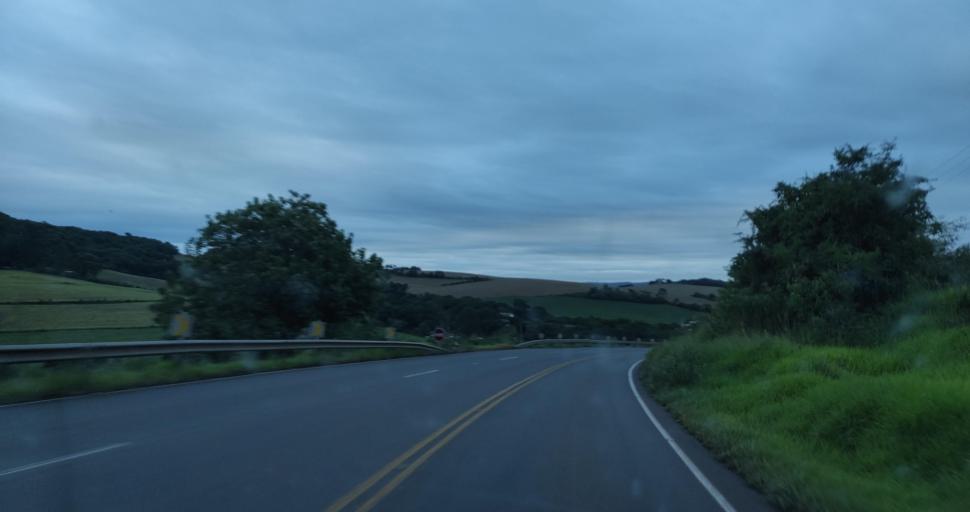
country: BR
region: Santa Catarina
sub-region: Xanxere
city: Xanxere
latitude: -26.7167
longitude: -52.4119
